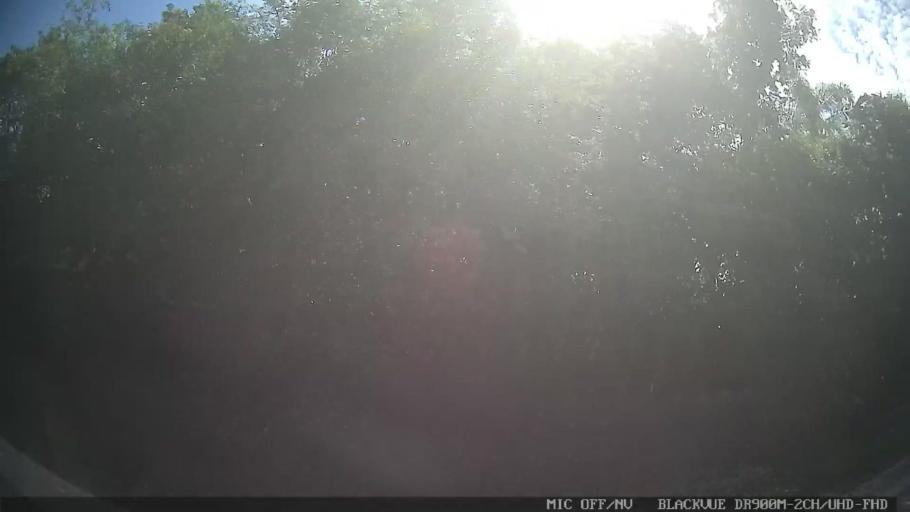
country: BR
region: Sao Paulo
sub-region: Porto Feliz
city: Porto Feliz
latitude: -23.2235
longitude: -47.5713
